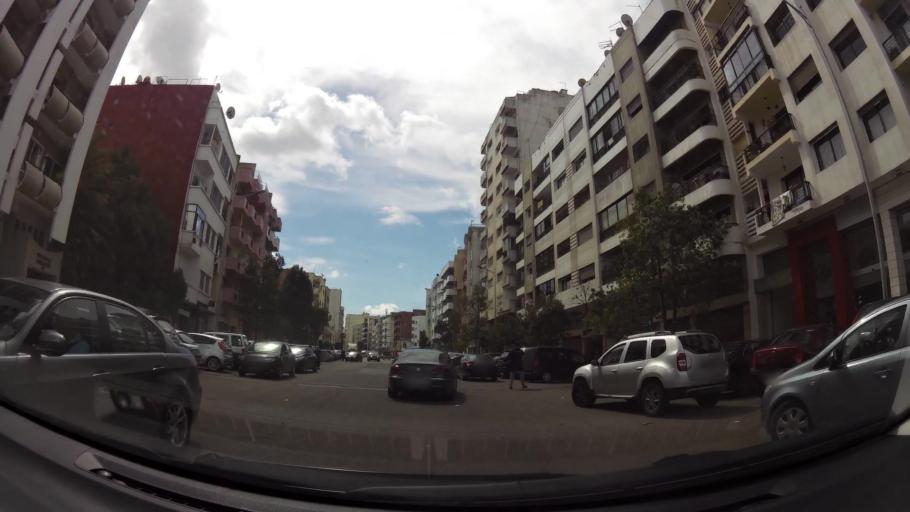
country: MA
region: Grand Casablanca
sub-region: Casablanca
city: Casablanca
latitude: 33.5834
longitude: -7.6441
